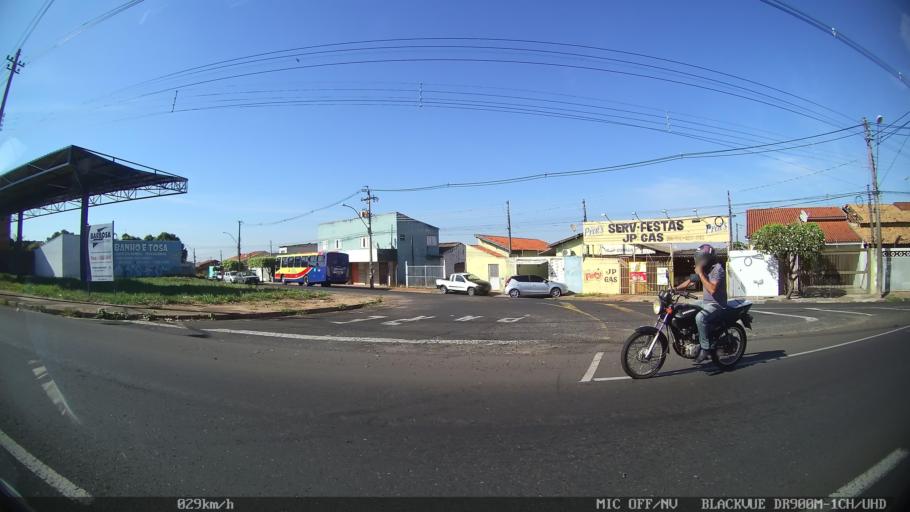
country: BR
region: Sao Paulo
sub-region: Sao Jose Do Rio Preto
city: Sao Jose do Rio Preto
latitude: -20.7717
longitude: -49.3921
